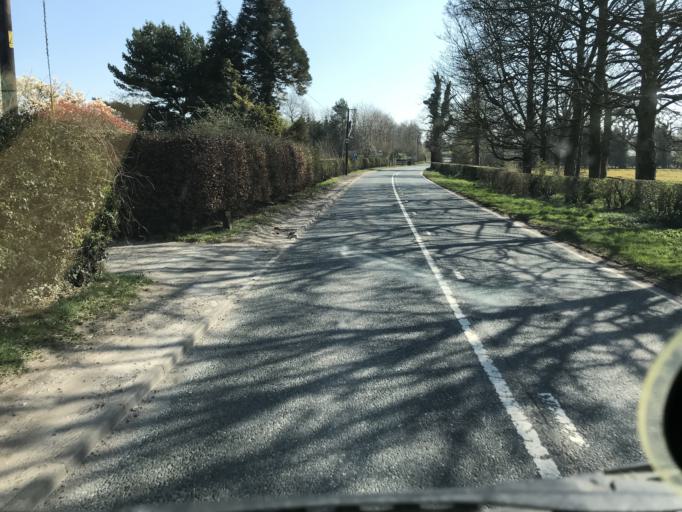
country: GB
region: England
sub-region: Cheshire East
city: Mobberley
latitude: 53.2829
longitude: -2.3190
